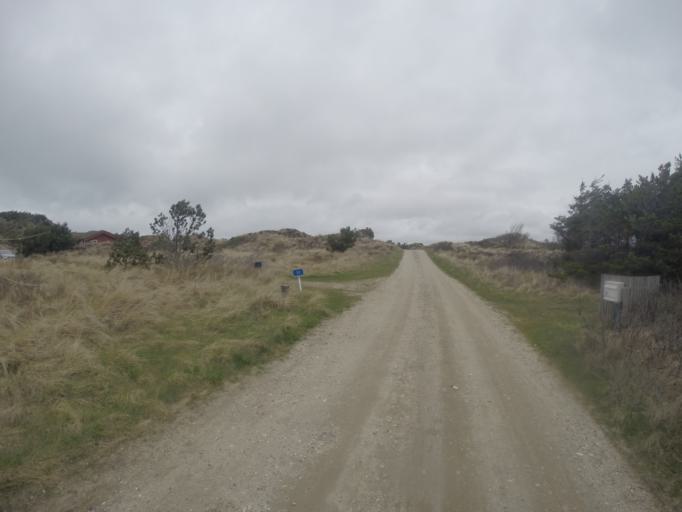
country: DK
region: North Denmark
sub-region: Thisted Kommune
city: Hurup
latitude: 56.8776
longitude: 8.3086
